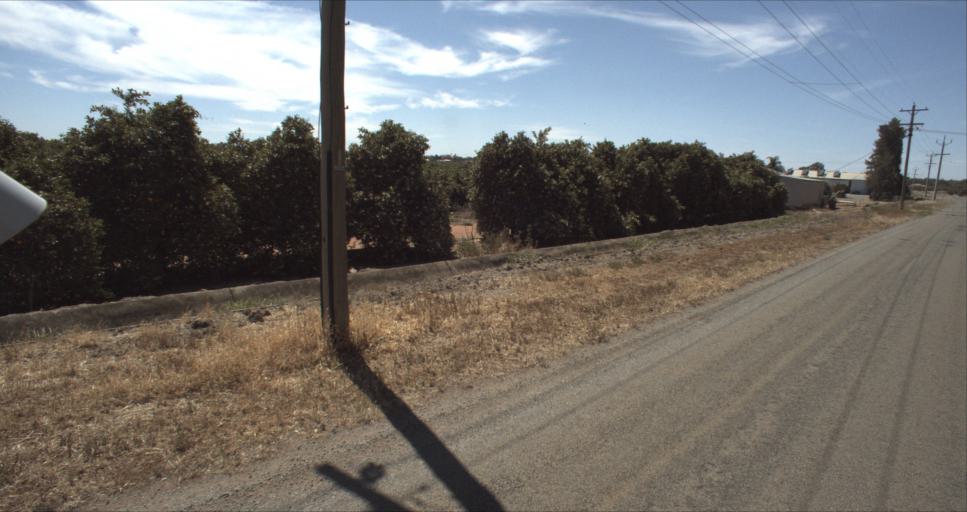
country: AU
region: New South Wales
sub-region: Leeton
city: Leeton
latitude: -34.6005
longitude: 146.4354
